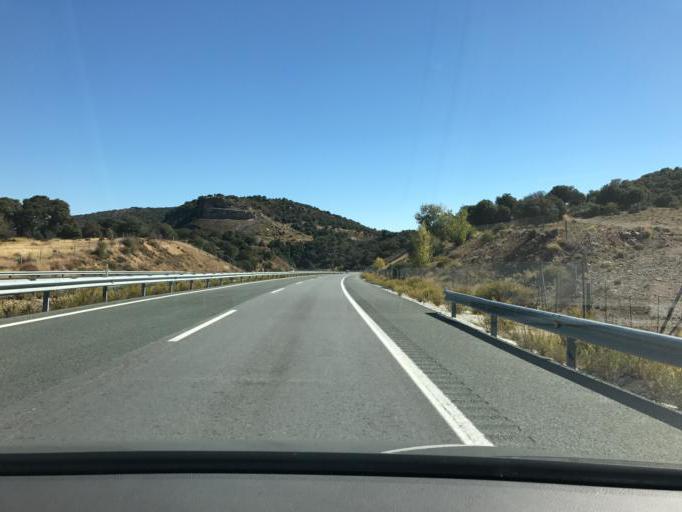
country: ES
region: Andalusia
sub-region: Provincia de Granada
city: Beas de Granada
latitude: 37.2993
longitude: -3.4402
